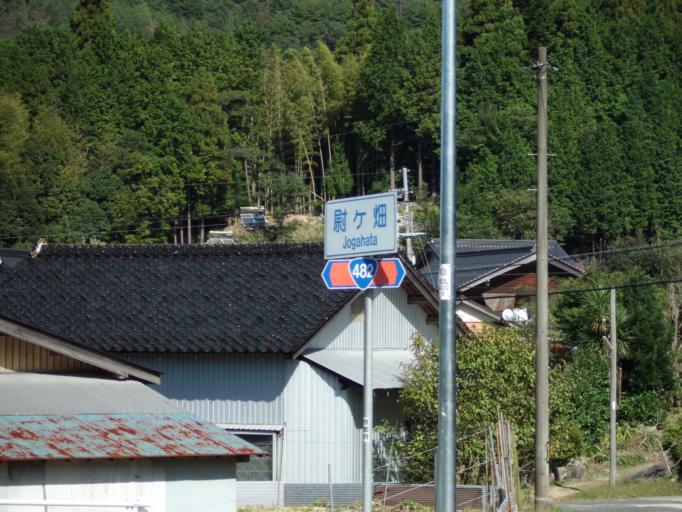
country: JP
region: Hyogo
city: Toyooka
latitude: 35.5445
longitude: 134.9774
